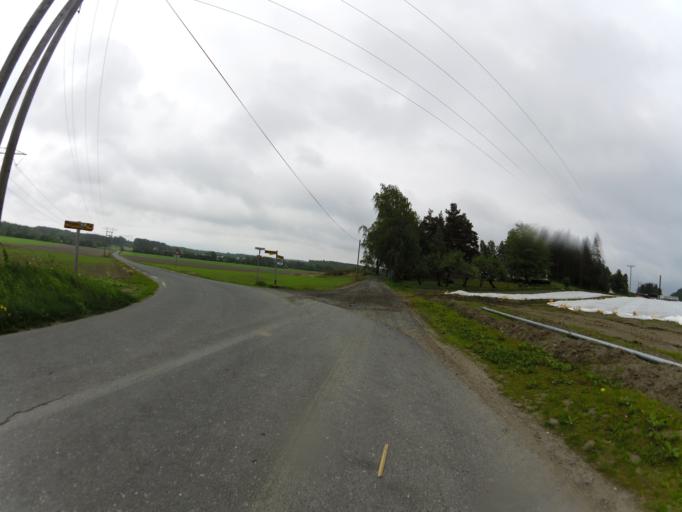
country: NO
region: Ostfold
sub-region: Rygge
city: Ryggebyen
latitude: 59.3563
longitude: 10.7310
